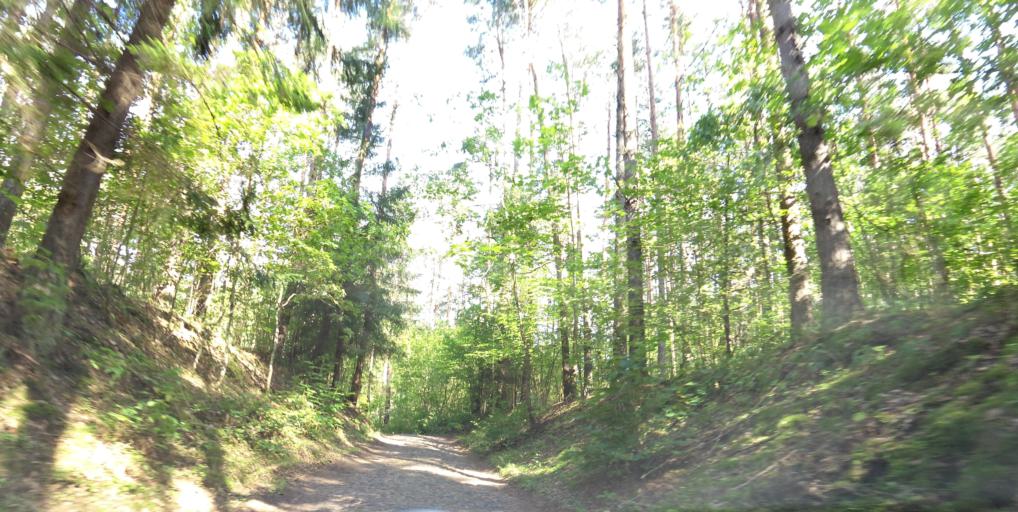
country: LT
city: Grigiskes
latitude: 54.7373
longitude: 25.0399
